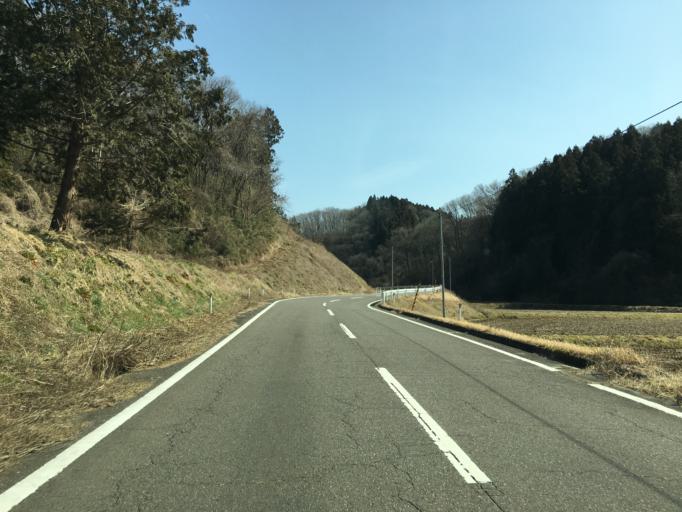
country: JP
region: Fukushima
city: Ishikawa
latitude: 37.1054
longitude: 140.4283
